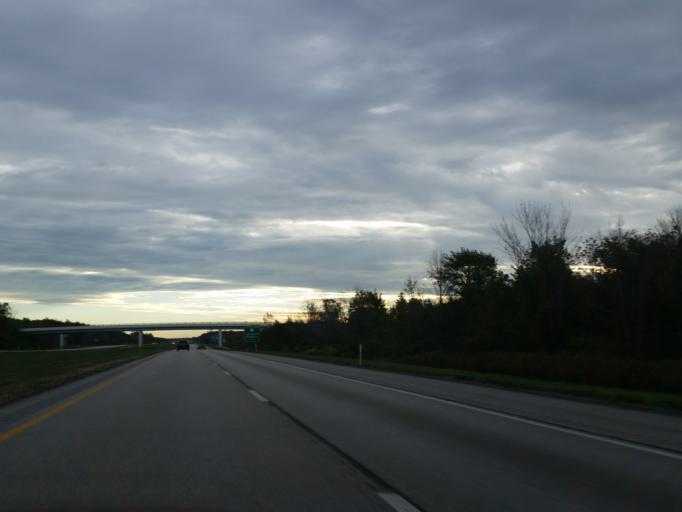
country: US
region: Ohio
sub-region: Ashtabula County
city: Conneaut
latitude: 41.9102
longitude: -80.5936
